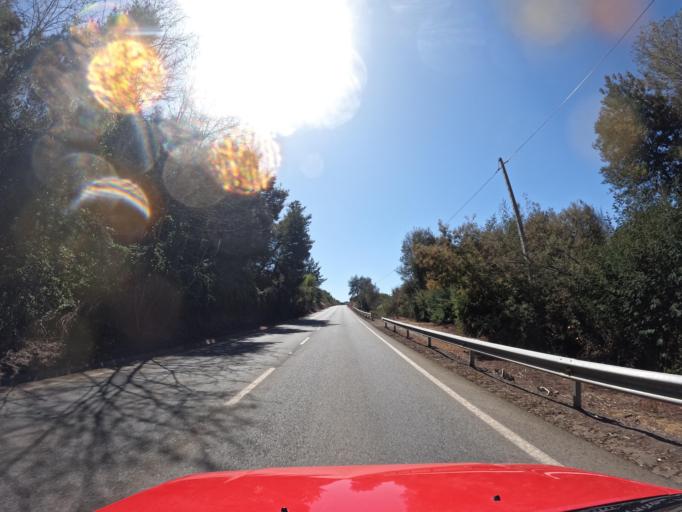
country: CL
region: Maule
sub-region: Provincia de Talca
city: San Clemente
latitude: -35.4536
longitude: -71.2695
